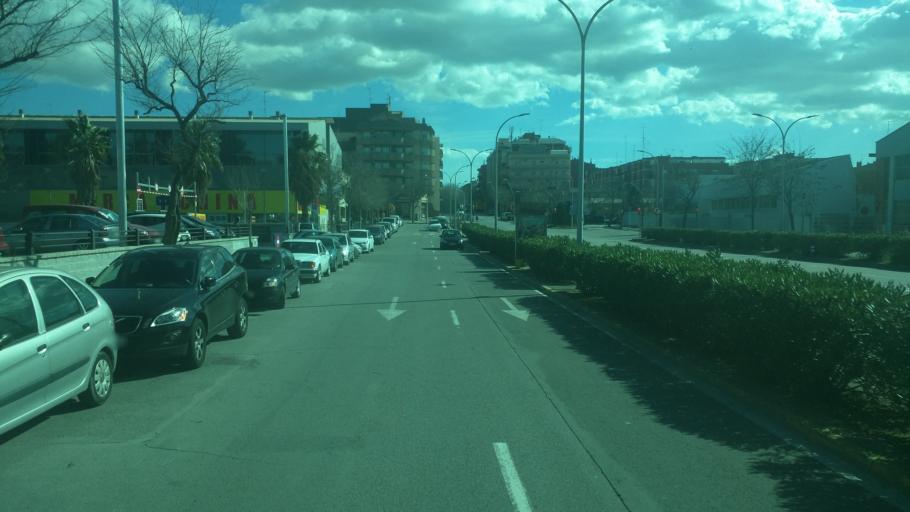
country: ES
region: Catalonia
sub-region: Provincia de Barcelona
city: Sant Feliu de Llobregat
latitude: 41.3869
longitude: 2.0400
